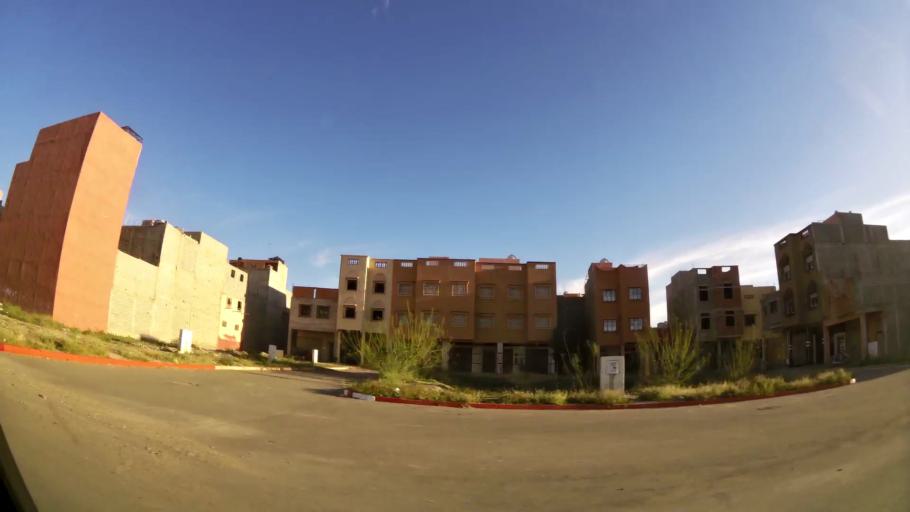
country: MA
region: Marrakech-Tensift-Al Haouz
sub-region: Marrakech
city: Marrakesh
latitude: 31.7429
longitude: -8.1211
